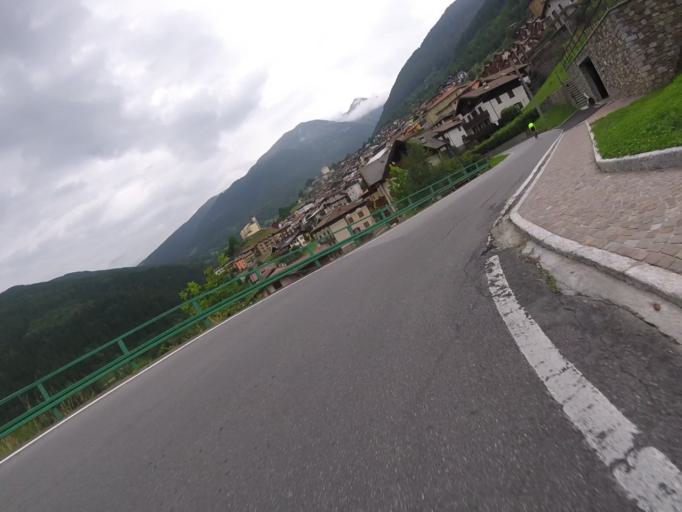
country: IT
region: Lombardy
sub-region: Provincia di Brescia
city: Monno
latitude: 46.2109
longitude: 10.3441
